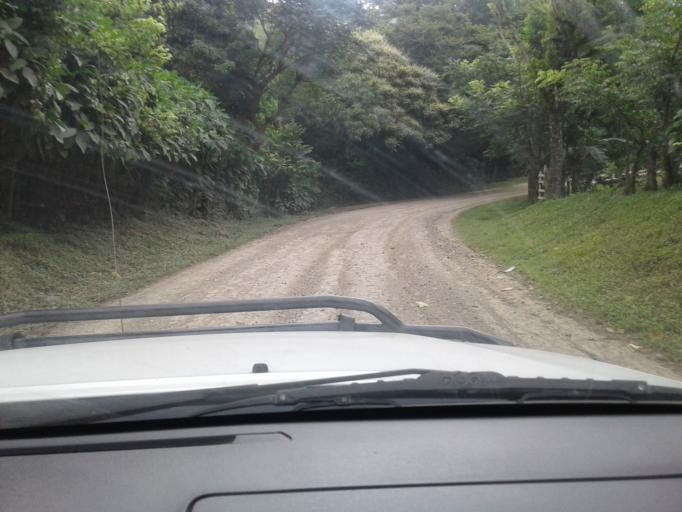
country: NI
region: Matagalpa
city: San Ramon
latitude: 12.9020
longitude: -85.8051
